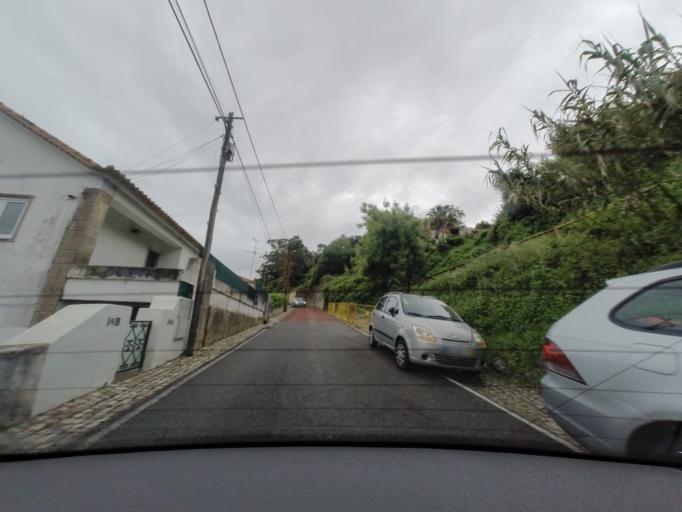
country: PT
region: Lisbon
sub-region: Sintra
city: Sintra
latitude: 38.7999
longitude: -9.3918
